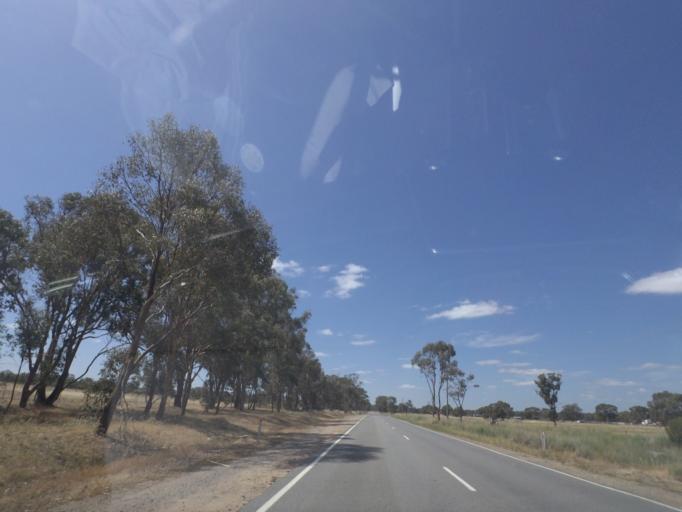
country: AU
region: Victoria
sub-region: Wangaratta
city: Wangaratta
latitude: -36.4188
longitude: 146.2628
